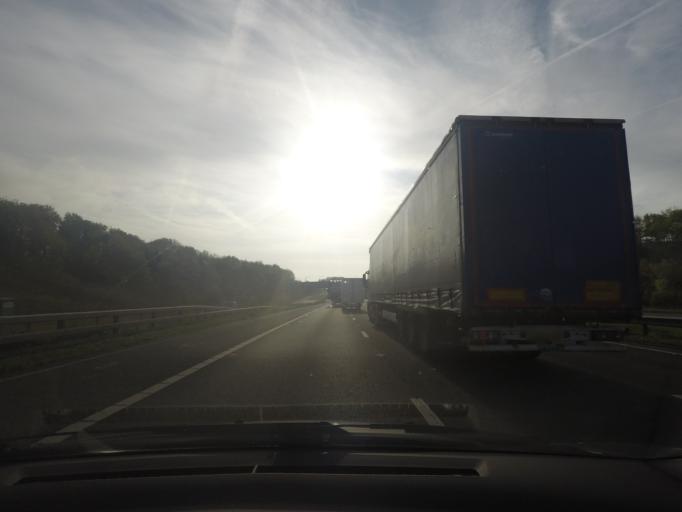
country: GB
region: England
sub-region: Barnsley
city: Dodworth
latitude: 53.5510
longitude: -1.5179
